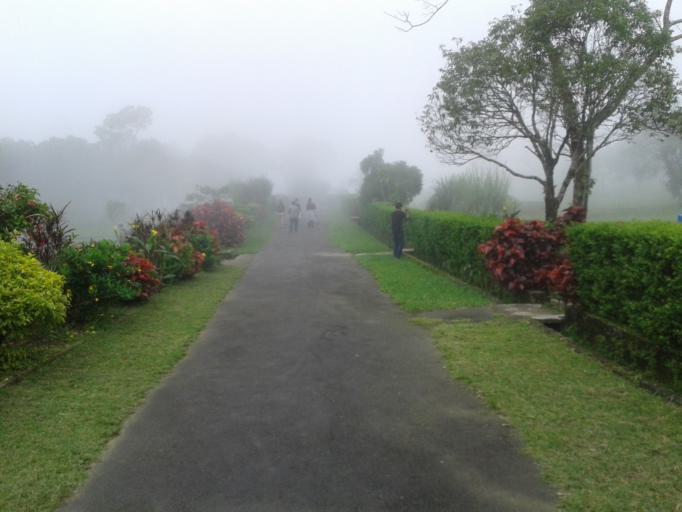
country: IN
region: Meghalaya
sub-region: East Khasi Hills
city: Cherrapunji
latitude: 25.2172
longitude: 91.7230
